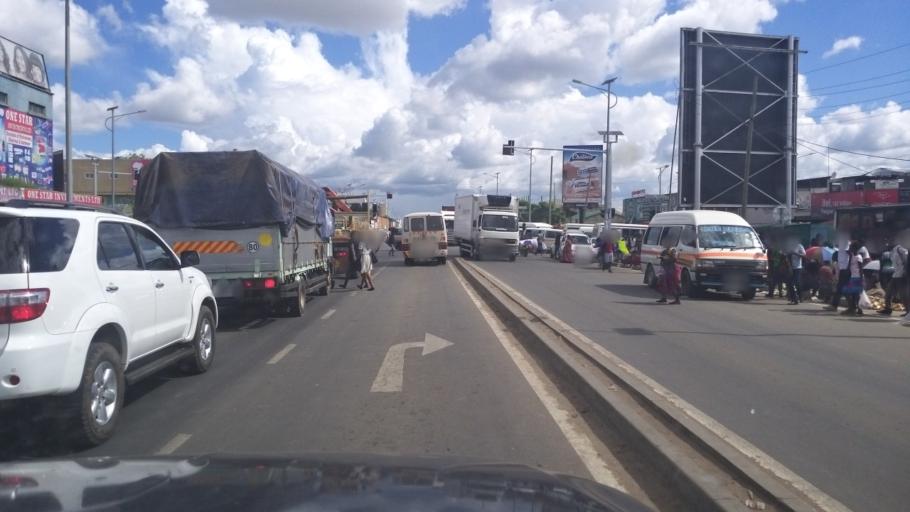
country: ZM
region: Lusaka
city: Lusaka
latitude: -15.4203
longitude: 28.2781
